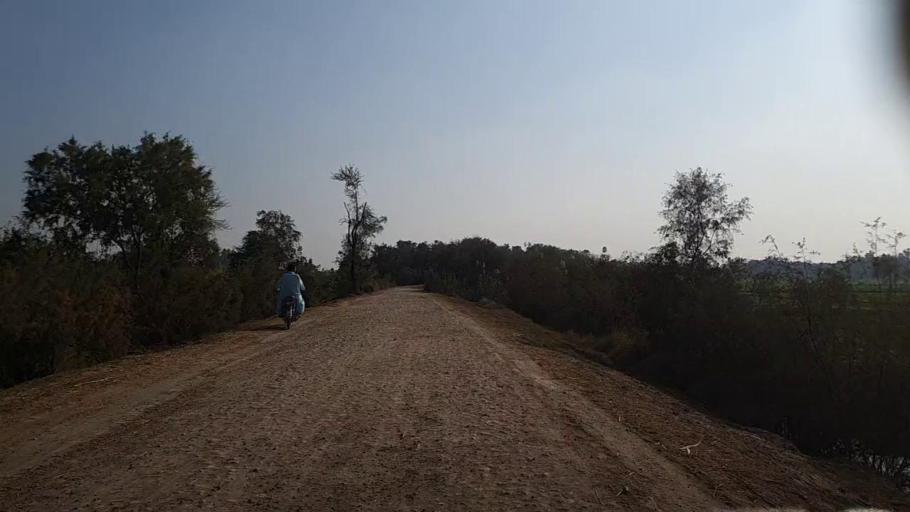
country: PK
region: Sindh
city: Mirpur Mathelo
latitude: 27.8983
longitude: 69.6068
